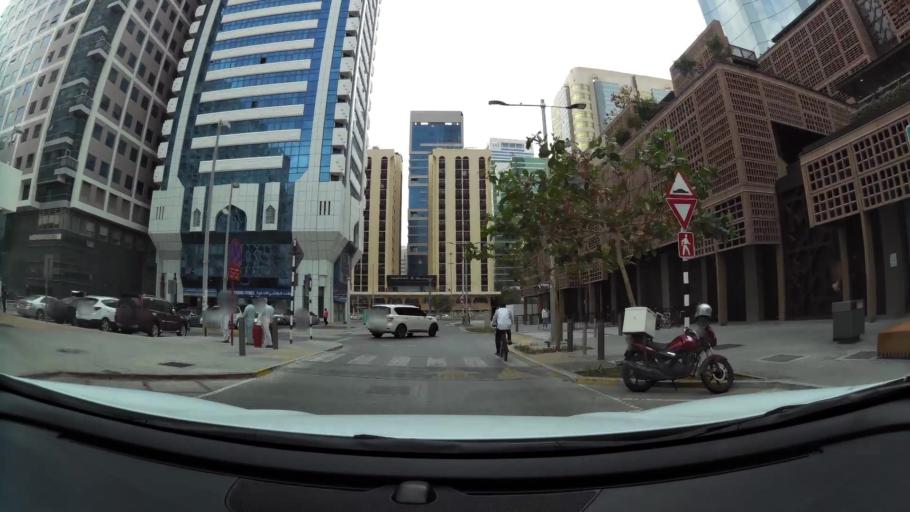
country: AE
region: Abu Dhabi
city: Abu Dhabi
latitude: 24.4875
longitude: 54.3584
